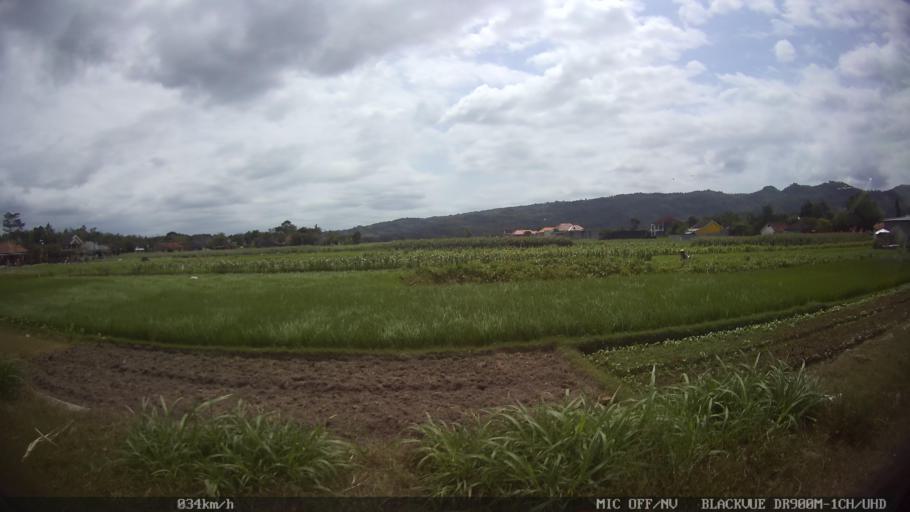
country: ID
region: Central Java
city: Candi Prambanan
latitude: -7.8145
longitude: 110.4986
